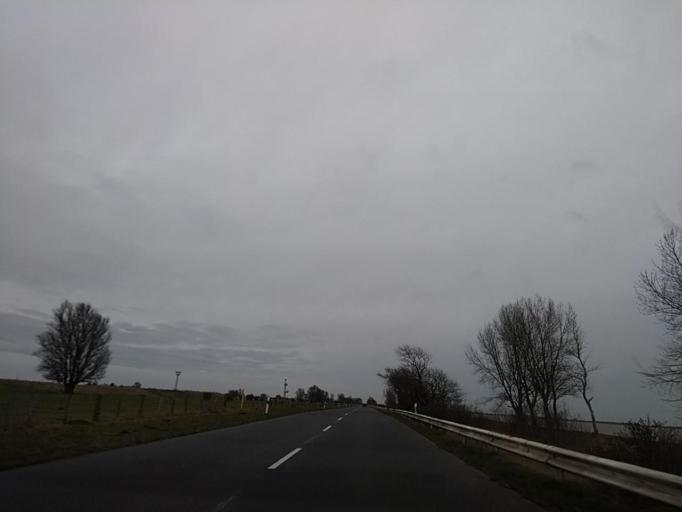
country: NL
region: Groningen
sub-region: Gemeente Delfzijl
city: Delfzijl
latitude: 53.3488
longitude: 7.0101
